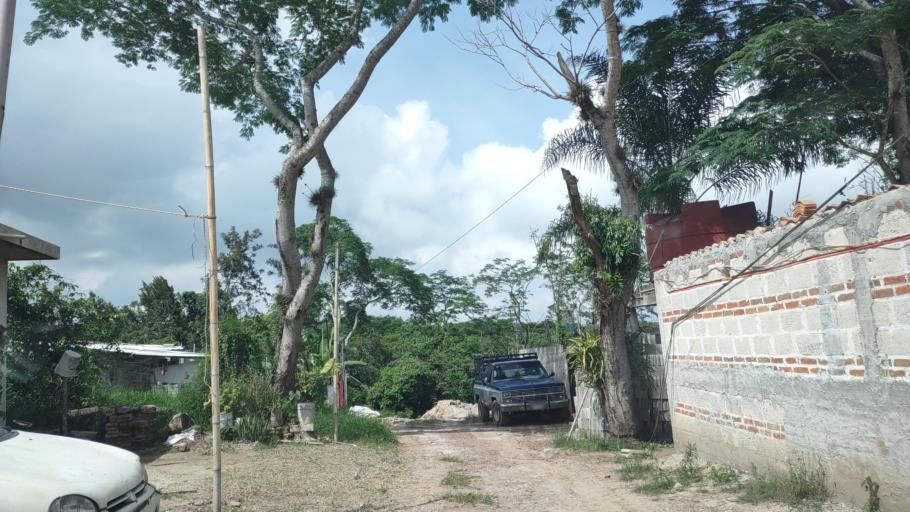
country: MX
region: Veracruz
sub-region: Emiliano Zapata
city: Jacarandas
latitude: 19.4715
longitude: -96.8379
